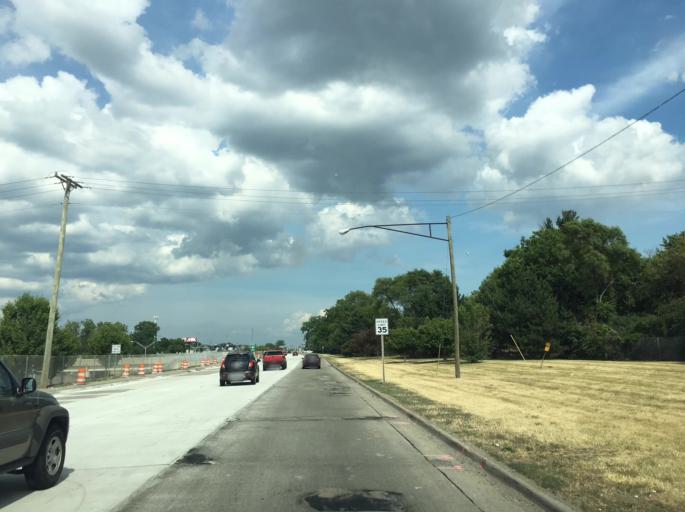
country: US
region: Michigan
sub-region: Macomb County
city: Utica
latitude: 42.6243
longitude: -83.0515
